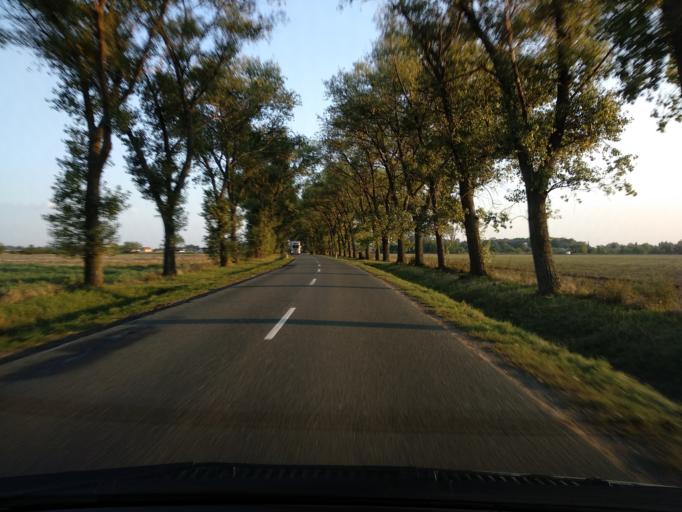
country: PL
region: Lower Silesian Voivodeship
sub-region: Powiat strzelinski
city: Strzelin
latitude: 50.8779
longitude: 17.0631
